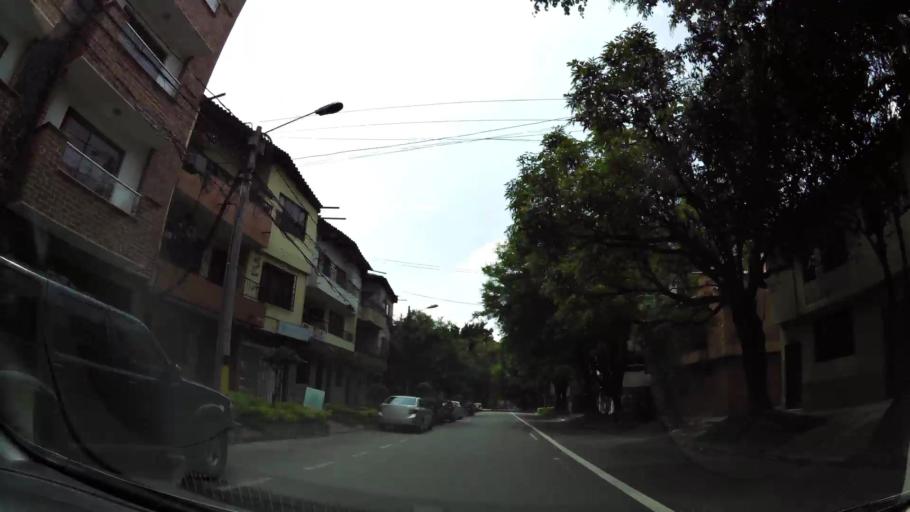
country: CO
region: Antioquia
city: Envigado
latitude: 6.1683
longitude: -75.5918
